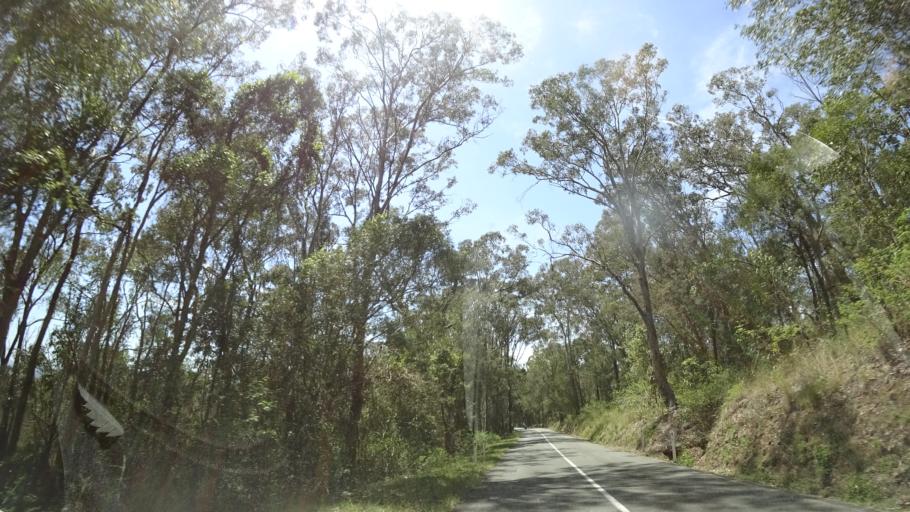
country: AU
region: Queensland
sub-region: Moreton Bay
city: Samford Valley
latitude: -27.4176
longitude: 152.8358
